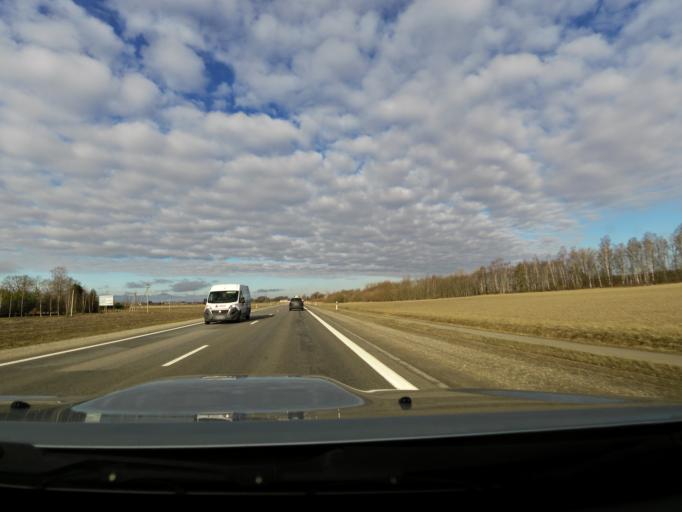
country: LT
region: Panevezys
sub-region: Panevezys City
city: Panevezys
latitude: 55.7407
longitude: 24.1881
